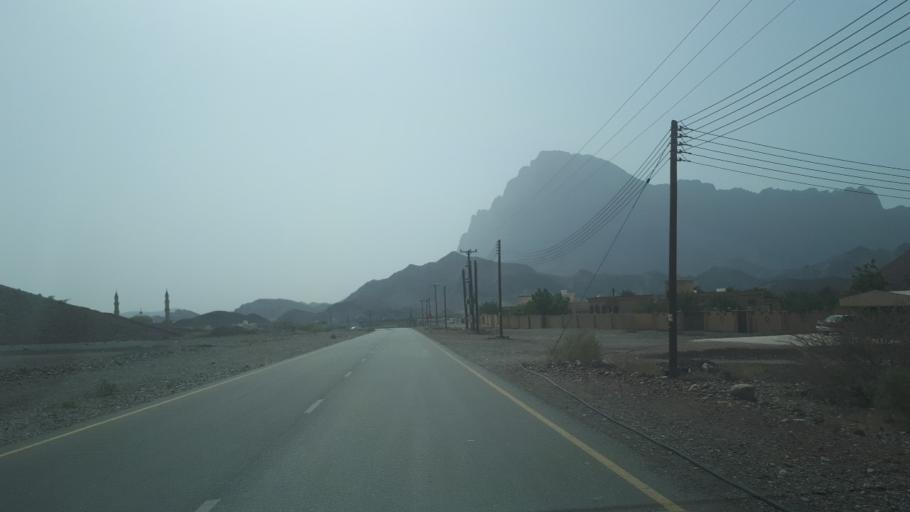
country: OM
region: Muhafazat ad Dakhiliyah
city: Bahla'
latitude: 23.2267
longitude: 57.0547
